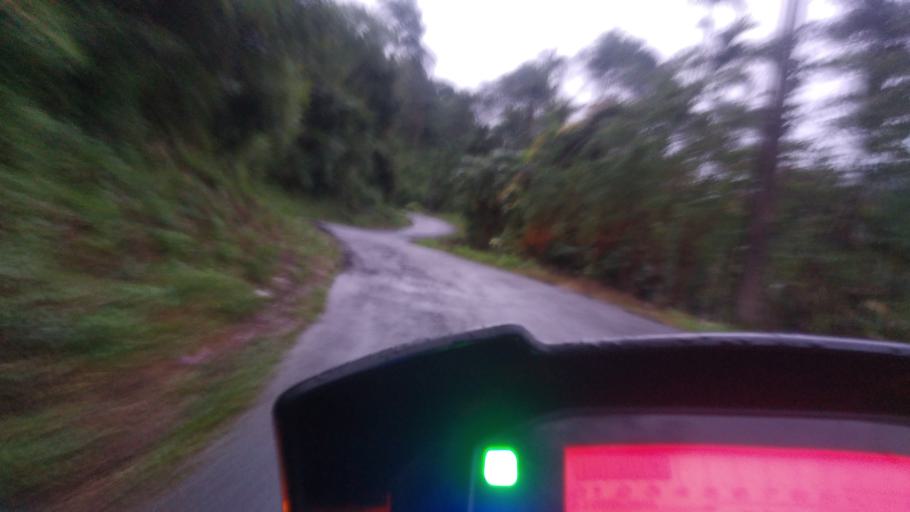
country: IN
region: Kerala
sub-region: Kottayam
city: Erattupetta
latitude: 9.5444
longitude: 76.9694
